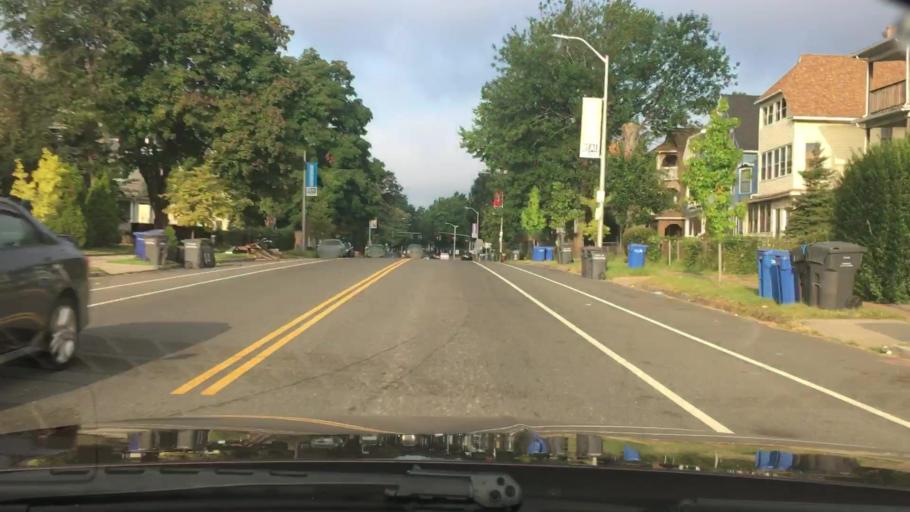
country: US
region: Connecticut
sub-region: Hartford County
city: Hartford
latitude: 41.7610
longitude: -72.7042
